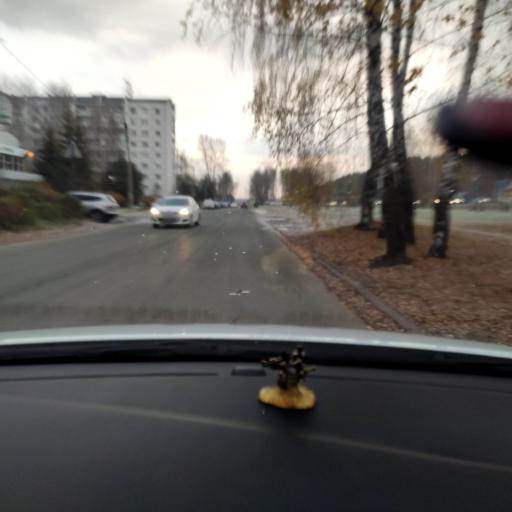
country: RU
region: Tatarstan
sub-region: Zelenodol'skiy Rayon
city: Zelenodolsk
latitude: 55.8506
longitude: 48.5639
